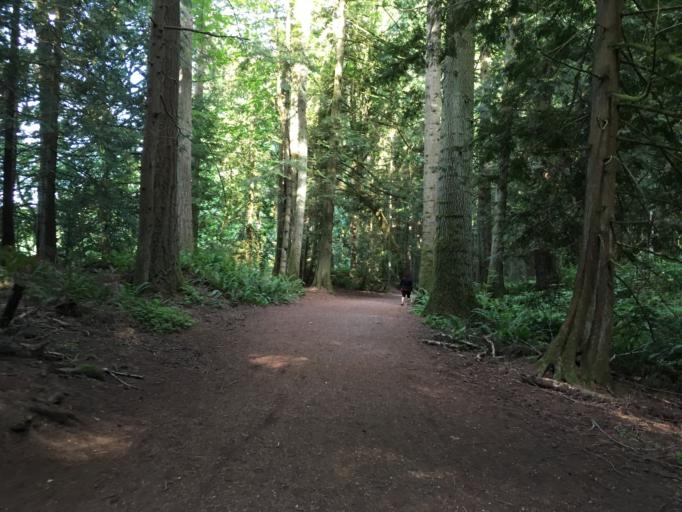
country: US
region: Washington
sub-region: Whatcom County
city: Bellingham
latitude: 48.7027
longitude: -122.4620
